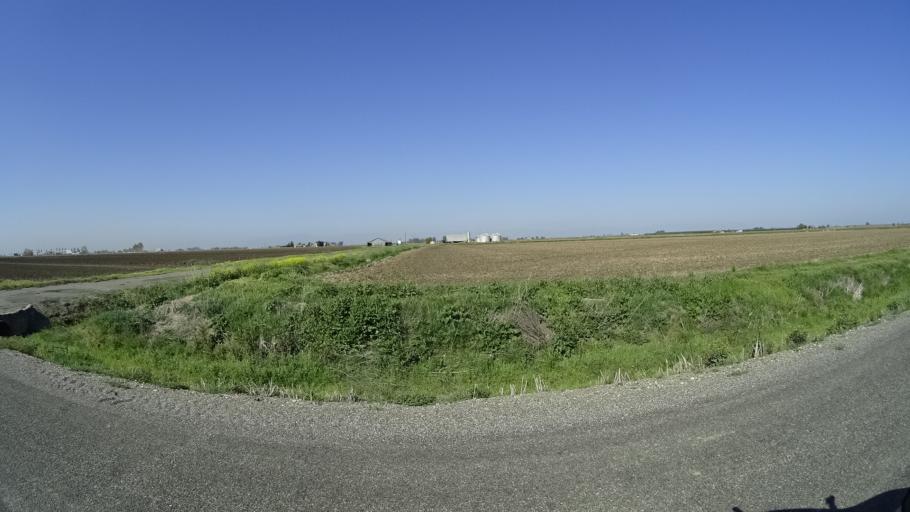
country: US
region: California
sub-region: Glenn County
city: Hamilton City
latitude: 39.6021
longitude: -122.0274
